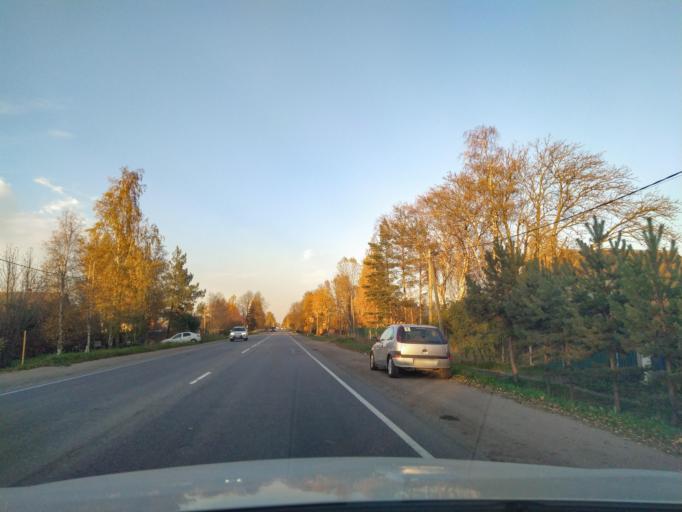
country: RU
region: Leningrad
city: Maloye Verevo
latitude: 59.6141
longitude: 30.2034
